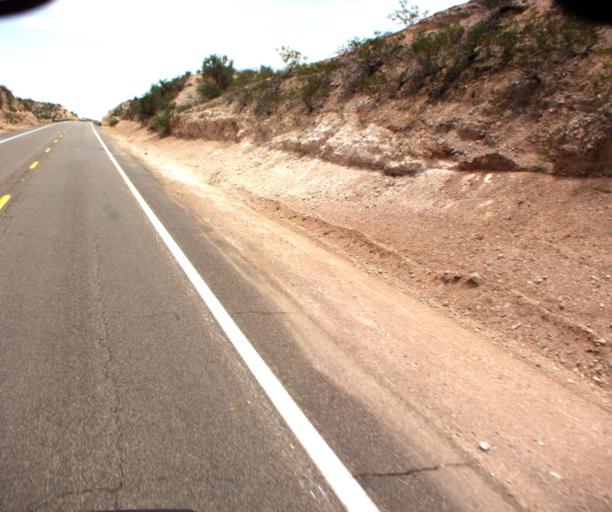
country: US
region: Arizona
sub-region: Graham County
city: Bylas
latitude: 33.2306
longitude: -110.2379
